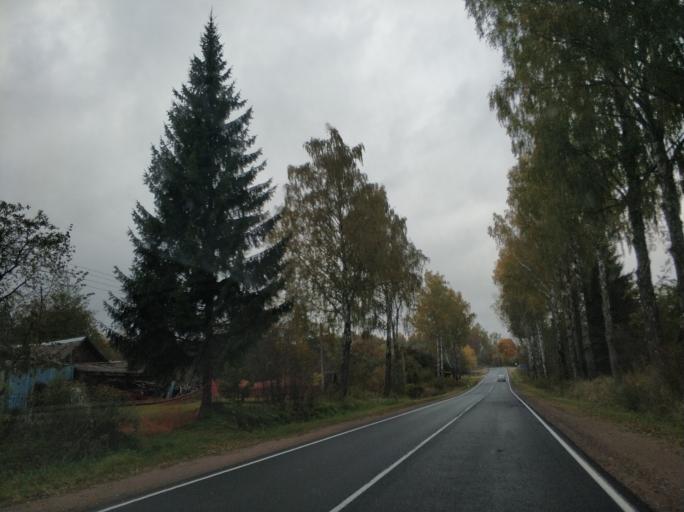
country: RU
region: Pskov
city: Opochka
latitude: 56.5522
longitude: 28.6335
